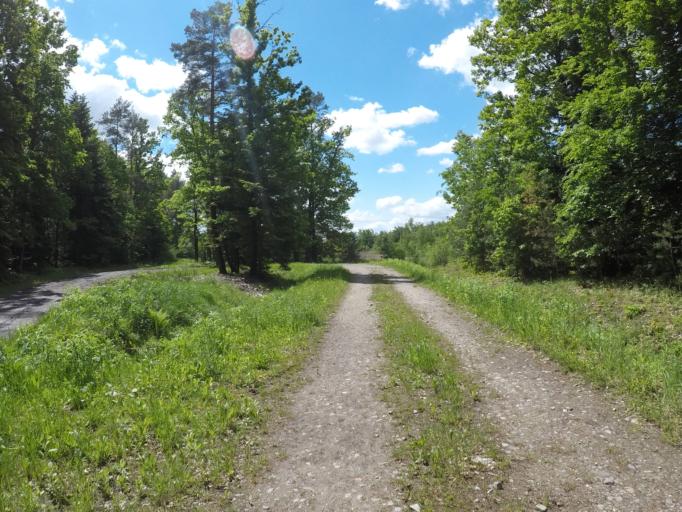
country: PL
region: Swietokrzyskie
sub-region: Powiat kielecki
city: Kostomloty Pierwsze
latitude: 50.9342
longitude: 20.6047
